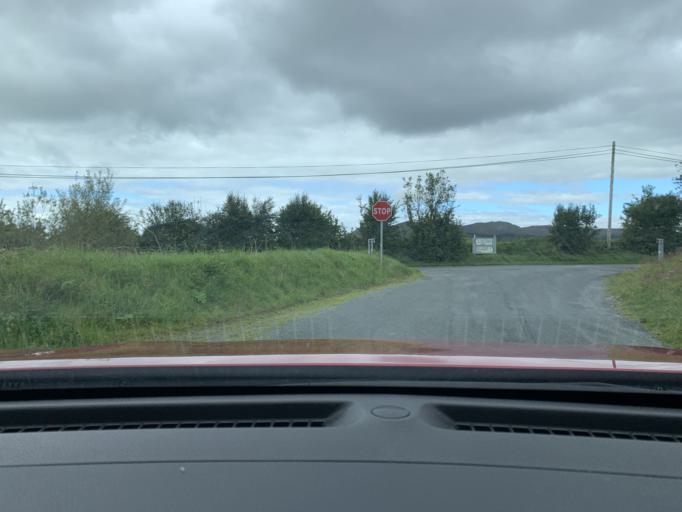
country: IE
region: Connaught
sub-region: Sligo
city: Collooney
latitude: 54.1887
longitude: -8.4528
